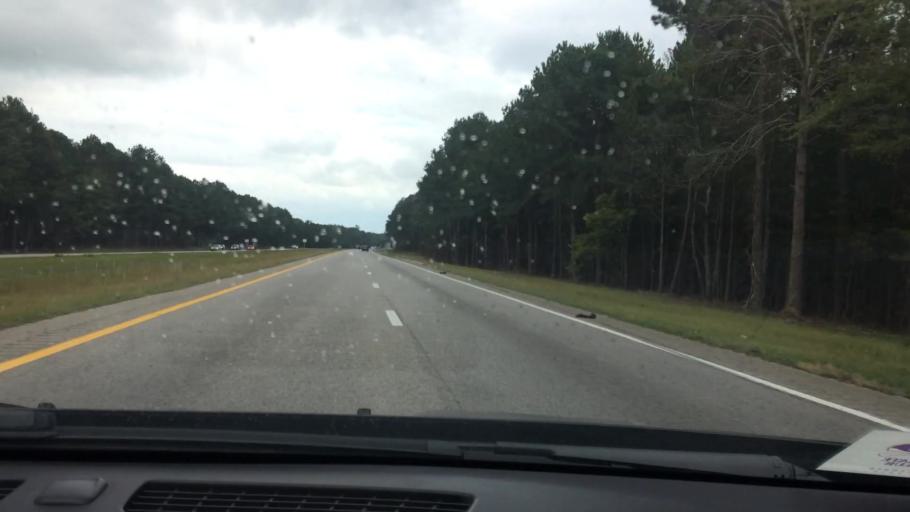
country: US
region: North Carolina
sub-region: Wake County
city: Zebulon
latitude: 35.8079
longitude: -78.2164
